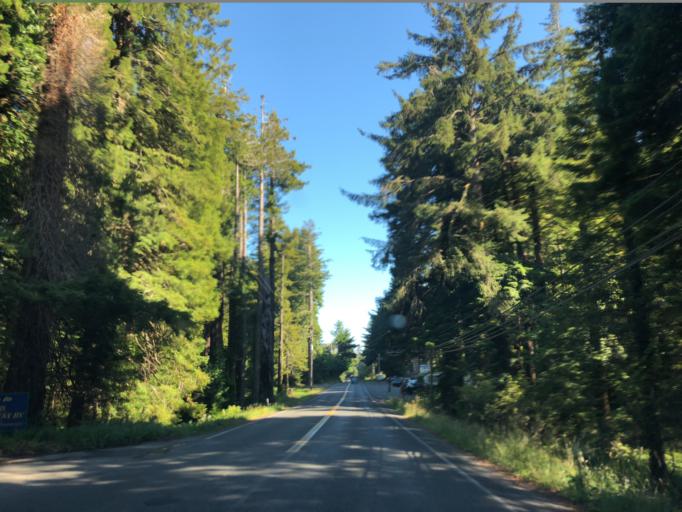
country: US
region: California
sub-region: Humboldt County
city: Westhaven-Moonstone
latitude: 41.0693
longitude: -124.1433
